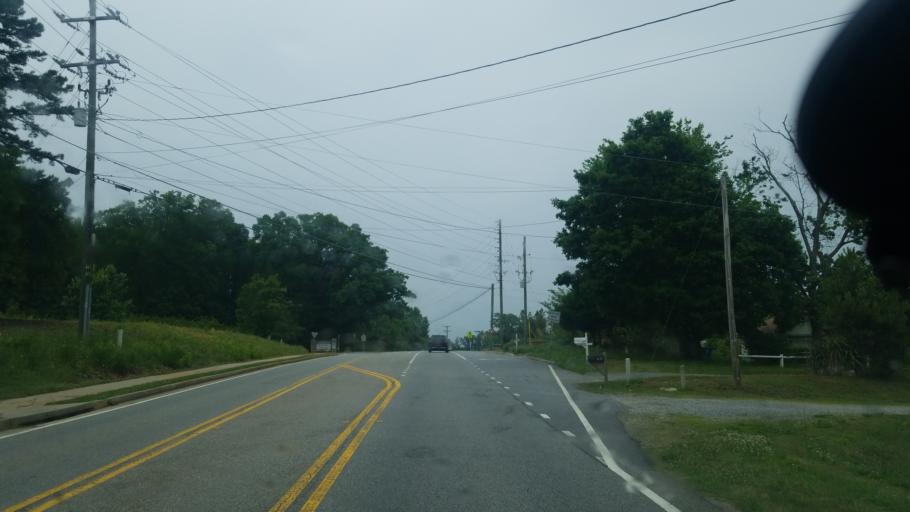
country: US
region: Georgia
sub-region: Gwinnett County
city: Suwanee
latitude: 34.1027
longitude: -84.1345
